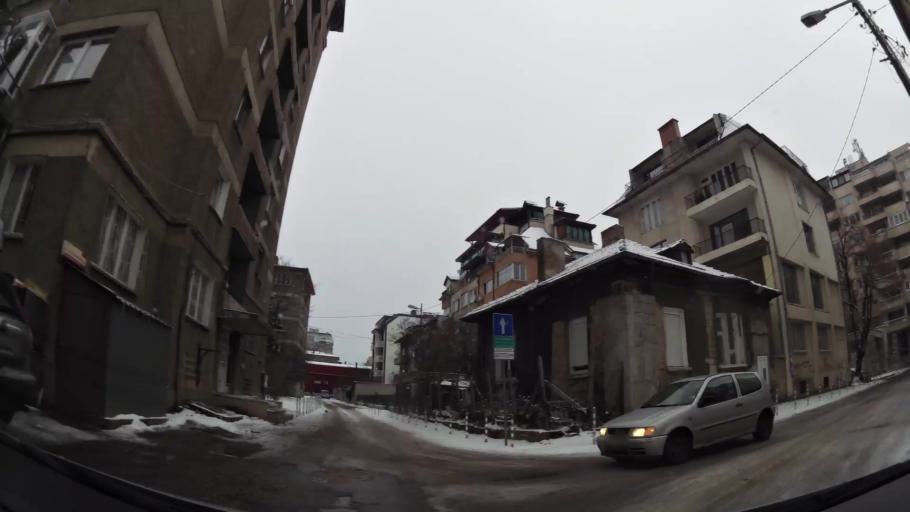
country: BG
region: Sofia-Capital
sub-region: Stolichna Obshtina
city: Sofia
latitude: 42.6986
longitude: 23.3420
